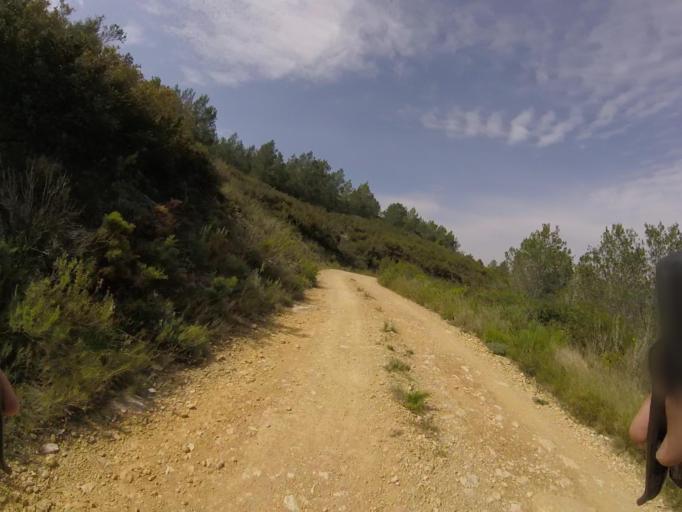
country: ES
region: Valencia
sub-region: Provincia de Castello
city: Cuevas de Vinroma
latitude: 40.2910
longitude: 0.1254
